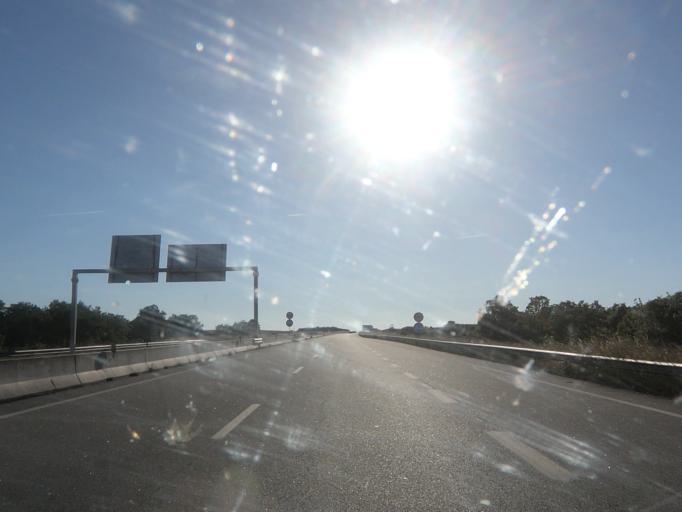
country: ES
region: Castille and Leon
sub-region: Provincia de Salamanca
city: Fuentes de Onoro
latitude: 40.6081
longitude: -6.9870
